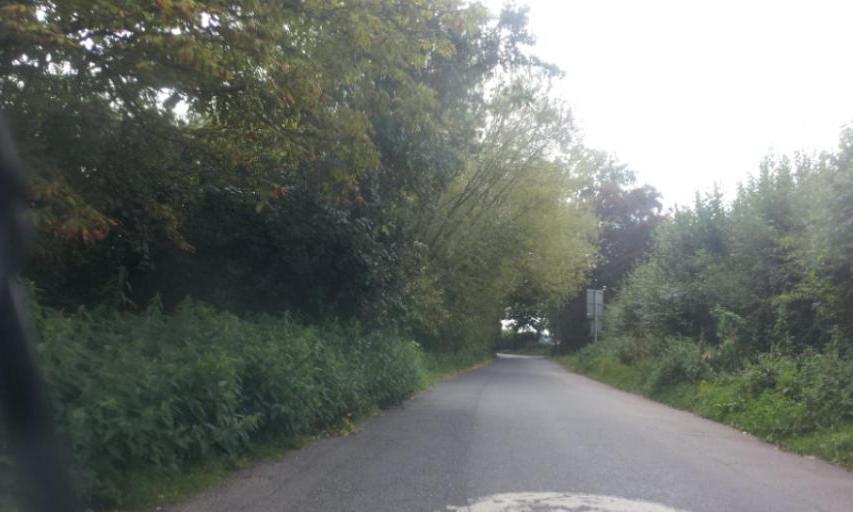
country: GB
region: England
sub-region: Kent
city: Yalding
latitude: 51.2050
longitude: 0.4181
